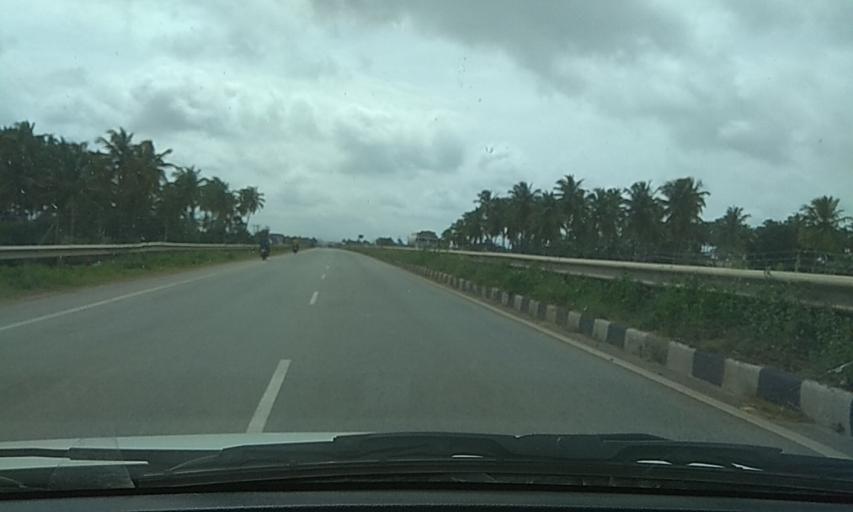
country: IN
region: Karnataka
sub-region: Davanagere
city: Harihar
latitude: 14.4517
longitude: 75.8753
